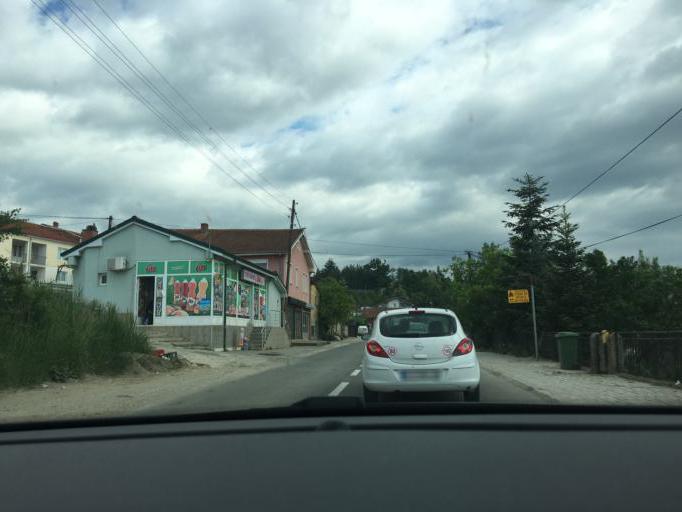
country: MK
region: Resen
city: Jankovec
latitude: 41.1107
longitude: 21.0117
